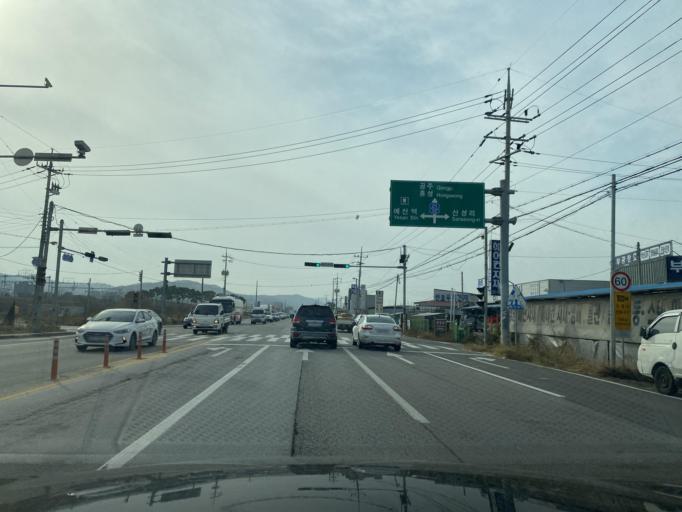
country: KR
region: Chungcheongnam-do
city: Yesan
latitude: 36.6913
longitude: 126.8278
